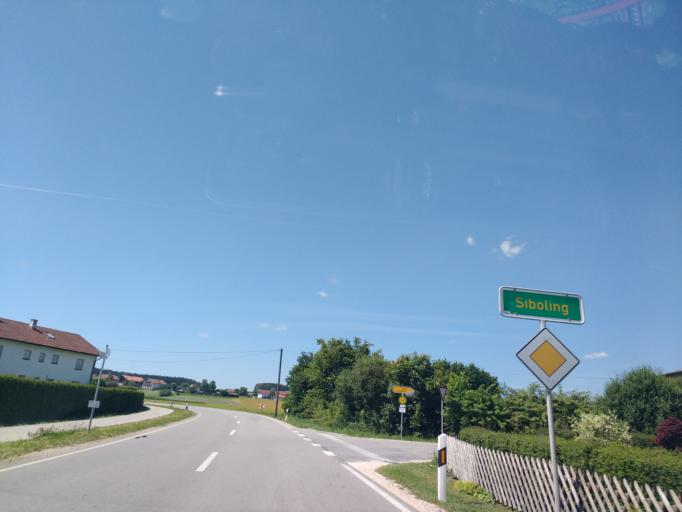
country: DE
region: Bavaria
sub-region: Upper Bavaria
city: Kienberg
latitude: 48.0310
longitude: 12.4407
